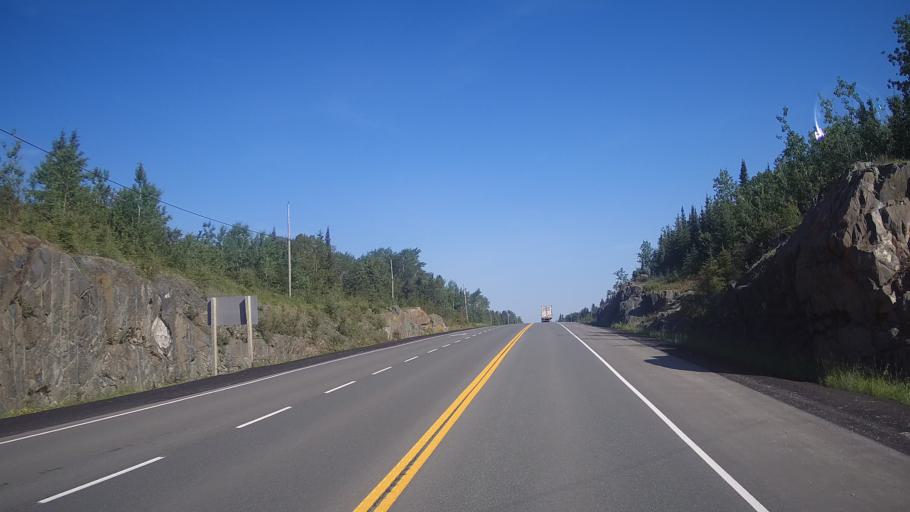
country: CA
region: Ontario
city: Dryden
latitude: 49.6550
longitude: -92.4770
